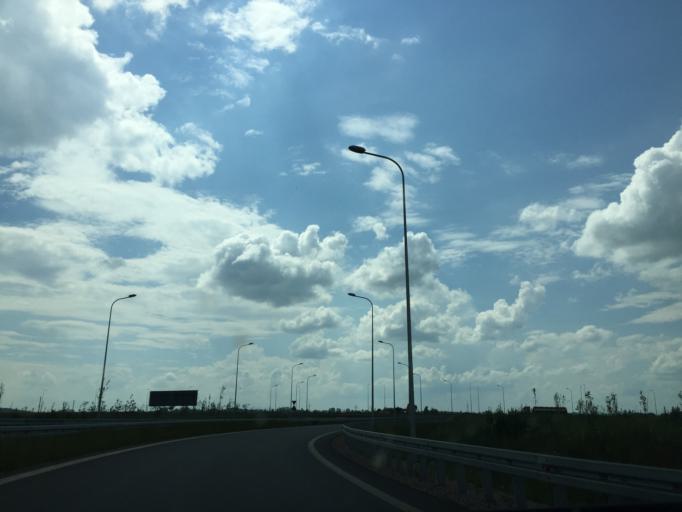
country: PL
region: Podlasie
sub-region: Suwalki
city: Suwalki
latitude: 54.0901
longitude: 22.8740
